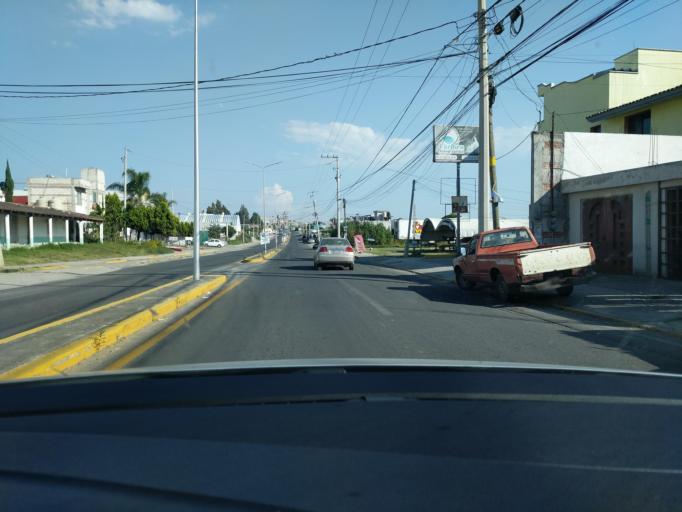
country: MX
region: Puebla
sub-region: San Gregorio Atzompa
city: Chipilo de Francisco Javier Mina
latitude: 19.0261
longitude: -98.3143
